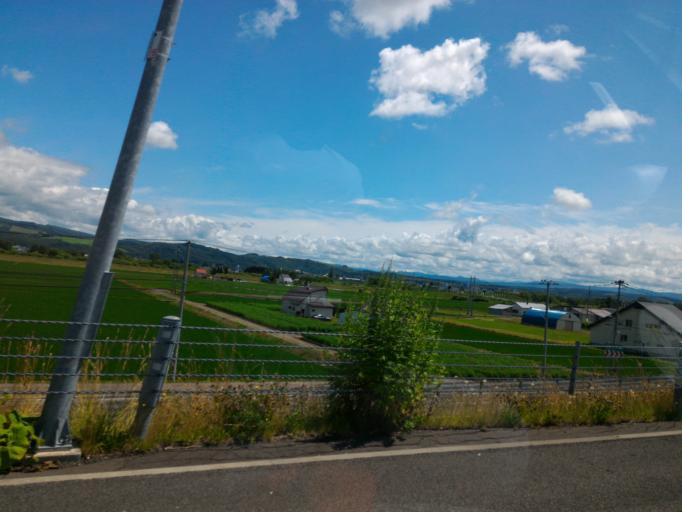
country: JP
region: Hokkaido
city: Nayoro
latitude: 44.3642
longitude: 142.4358
